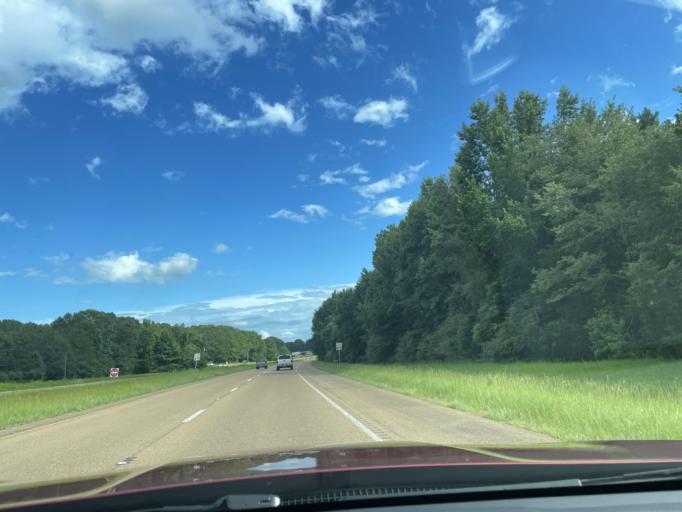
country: US
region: Mississippi
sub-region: Madison County
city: Flora
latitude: 32.5257
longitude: -90.3095
